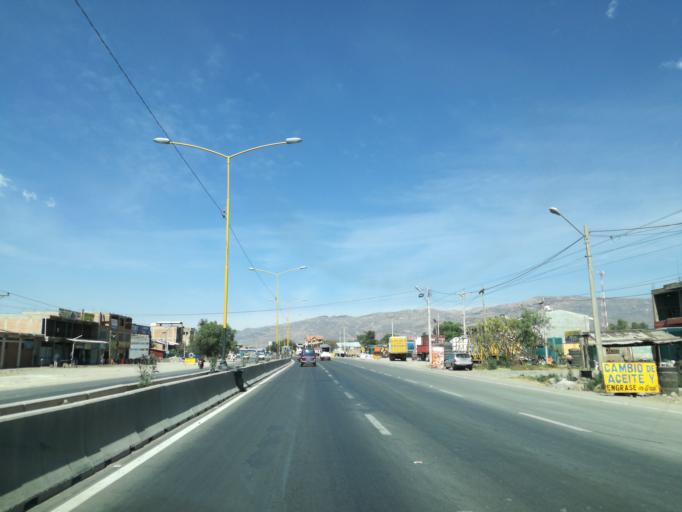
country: BO
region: Cochabamba
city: Sipe Sipe
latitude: -17.4101
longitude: -66.3325
